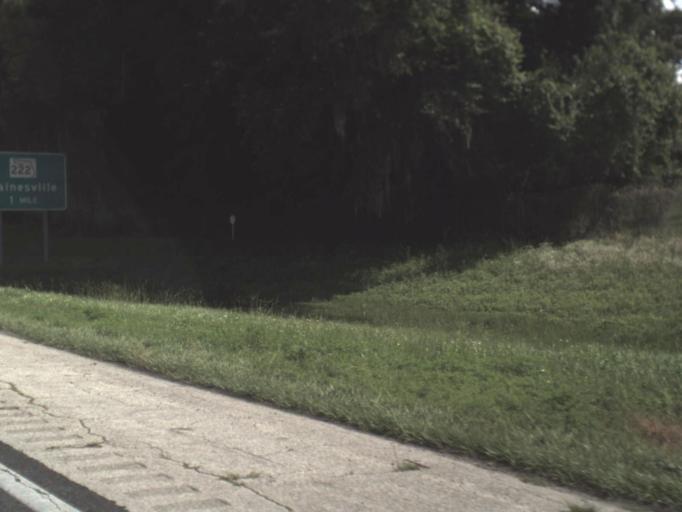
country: US
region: Florida
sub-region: Alachua County
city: Alachua
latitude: 29.6729
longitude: -82.4306
